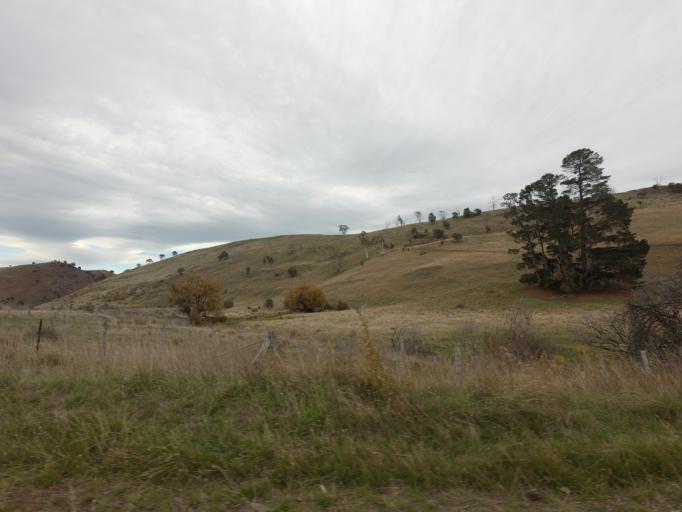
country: AU
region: Tasmania
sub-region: Derwent Valley
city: New Norfolk
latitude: -42.3667
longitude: 146.8425
